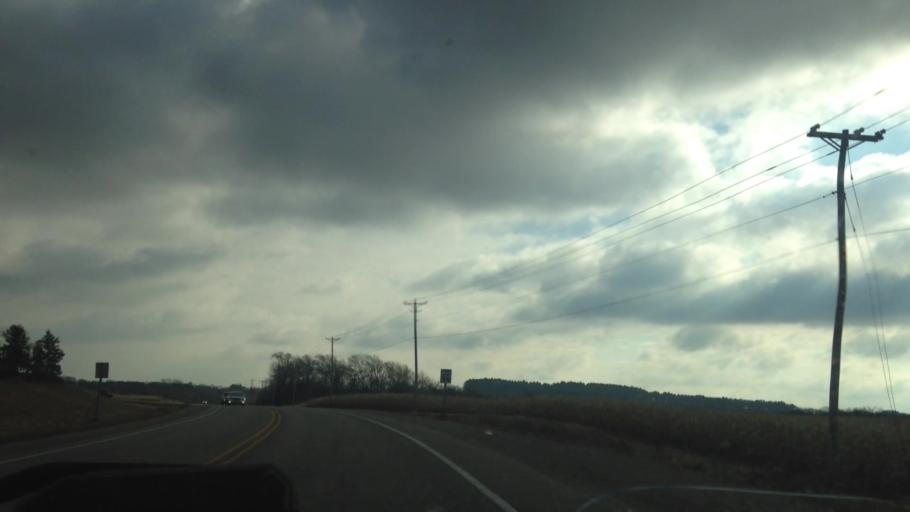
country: US
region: Wisconsin
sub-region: Dodge County
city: Beaver Dam
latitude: 43.4507
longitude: -88.7990
